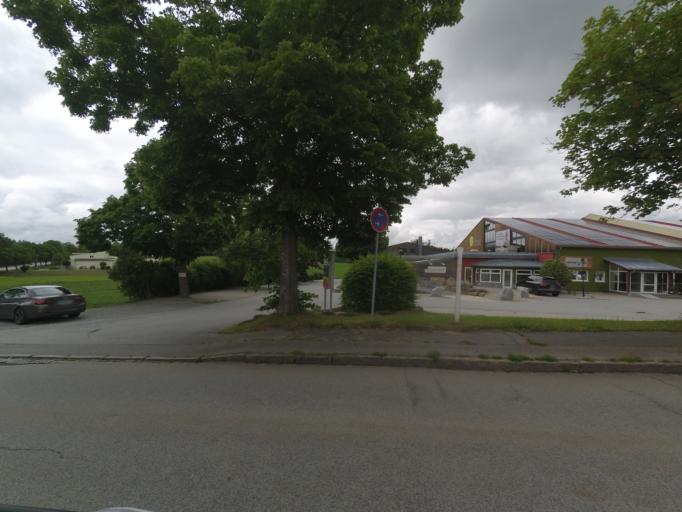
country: DE
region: Bavaria
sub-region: Lower Bavaria
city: Regen
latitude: 48.9745
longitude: 13.1191
